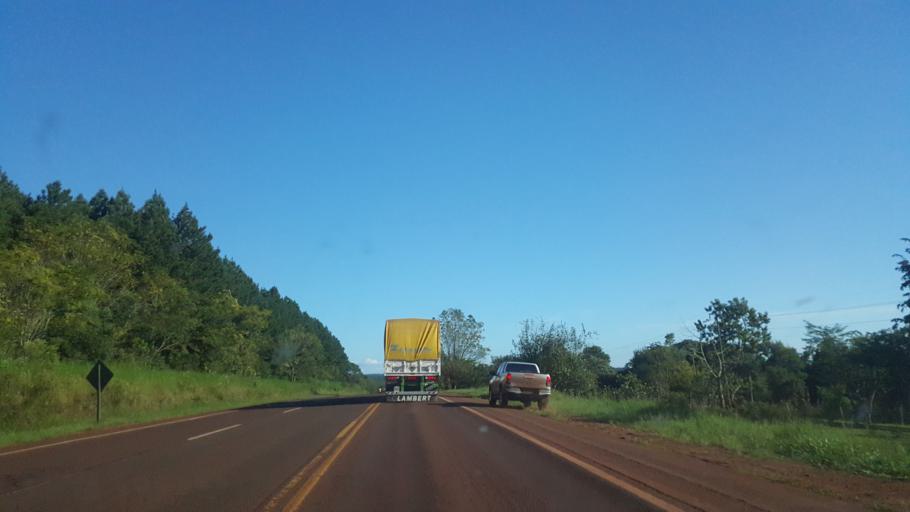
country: AR
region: Misiones
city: Puerto Esperanza
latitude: -26.1854
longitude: -54.5892
